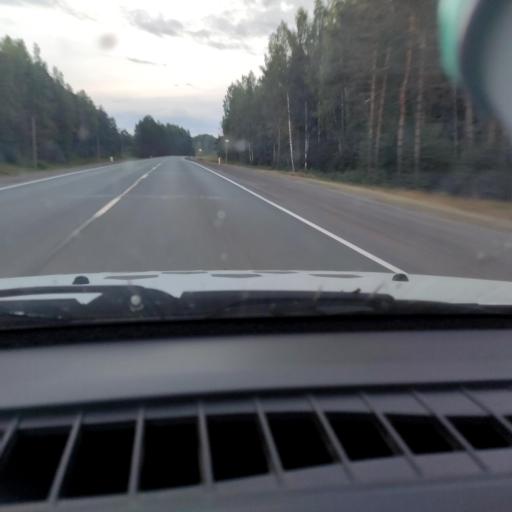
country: RU
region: Kirov
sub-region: Kirovo-Chepetskiy Rayon
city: Kirov
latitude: 58.7042
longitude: 49.6081
